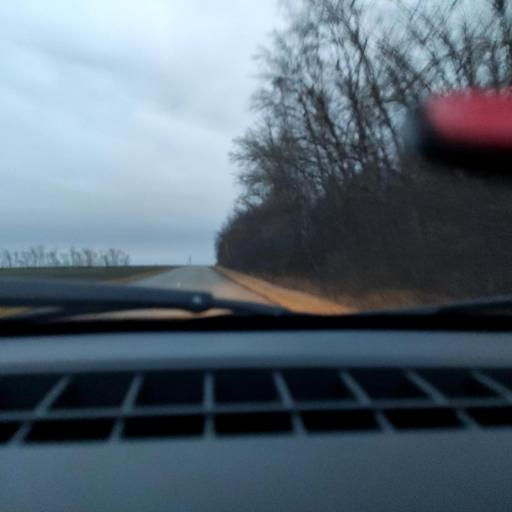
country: RU
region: Bashkortostan
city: Avdon
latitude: 54.5671
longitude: 55.6777
